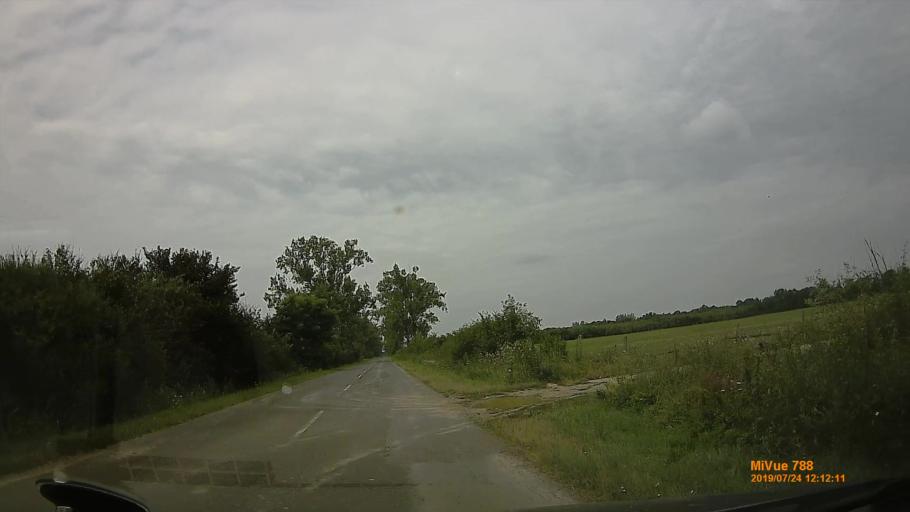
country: HU
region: Szabolcs-Szatmar-Bereg
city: Vasarosnameny
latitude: 48.1946
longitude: 22.3852
